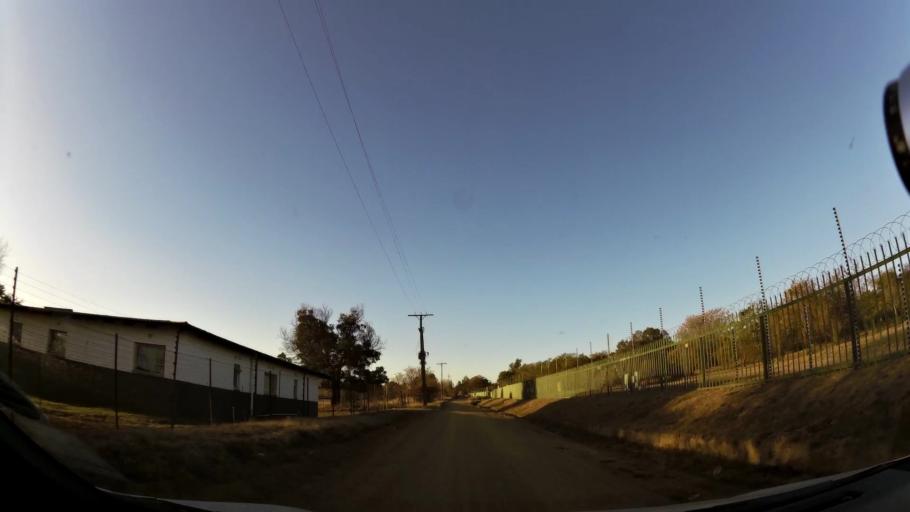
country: ZA
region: Gauteng
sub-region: City of Johannesburg Metropolitan Municipality
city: Diepsloot
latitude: -25.9401
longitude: 28.0414
